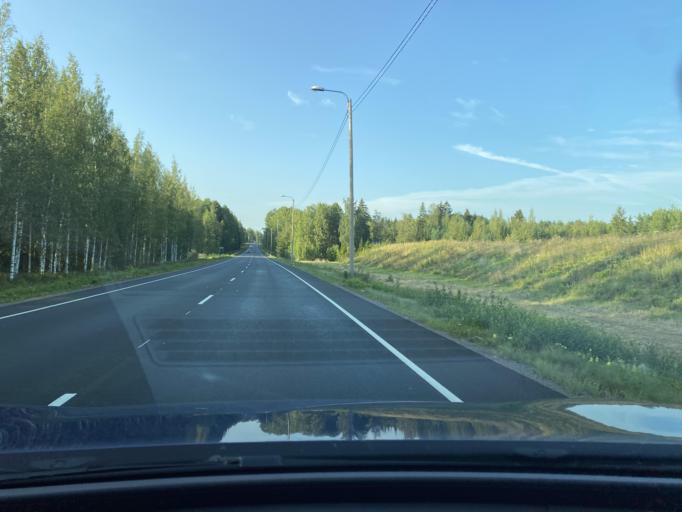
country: FI
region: Kymenlaakso
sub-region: Kouvola
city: Kouvola
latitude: 60.8883
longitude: 26.6047
